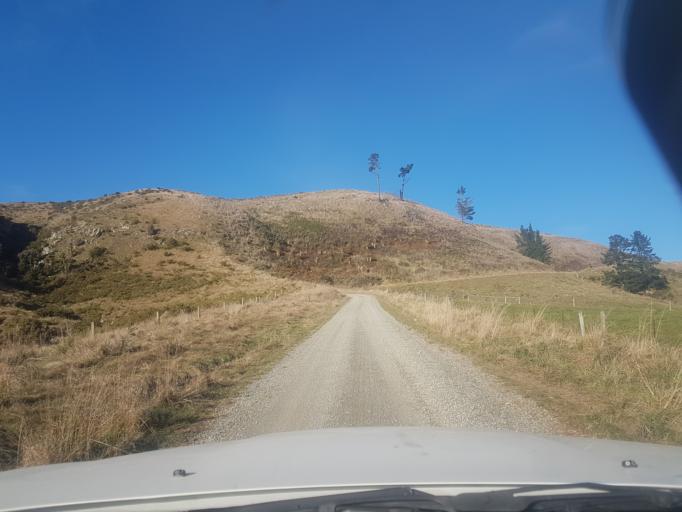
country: NZ
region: Canterbury
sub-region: Timaru District
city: Pleasant Point
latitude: -44.1660
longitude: 170.8792
